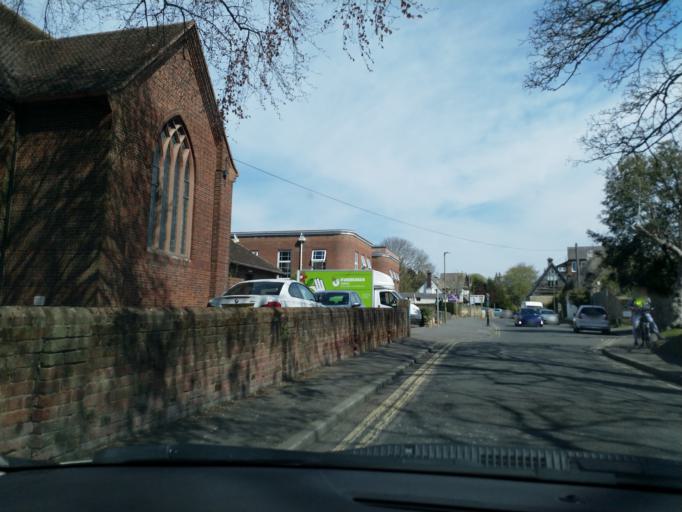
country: GB
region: England
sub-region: Oxfordshire
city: Cowley
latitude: 51.7347
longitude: -1.2130
